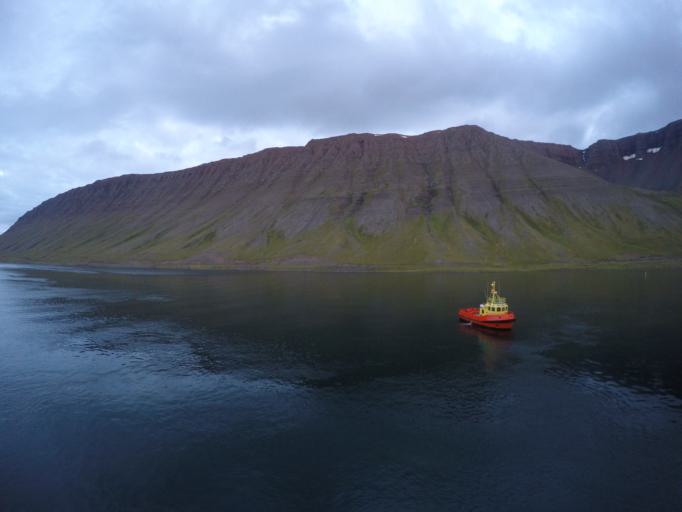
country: IS
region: Westfjords
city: Isafjoerdur
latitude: 66.0670
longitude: -23.1174
